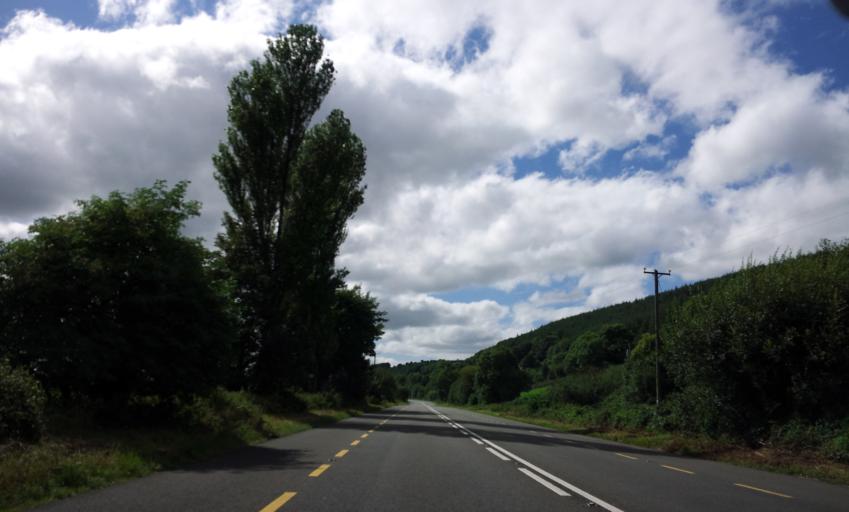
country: IE
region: Munster
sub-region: County Cork
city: Killumney
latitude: 51.8670
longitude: -8.7555
